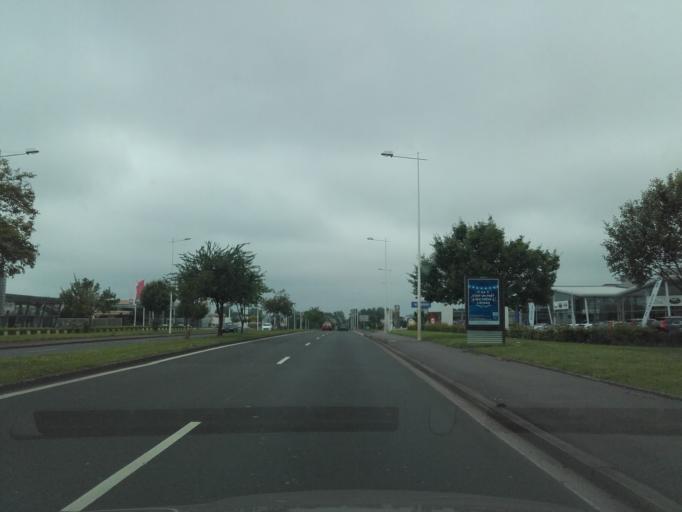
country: FR
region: Centre
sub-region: Departement d'Indre-et-Loire
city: Parcay-Meslay
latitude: 47.4255
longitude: 0.7111
